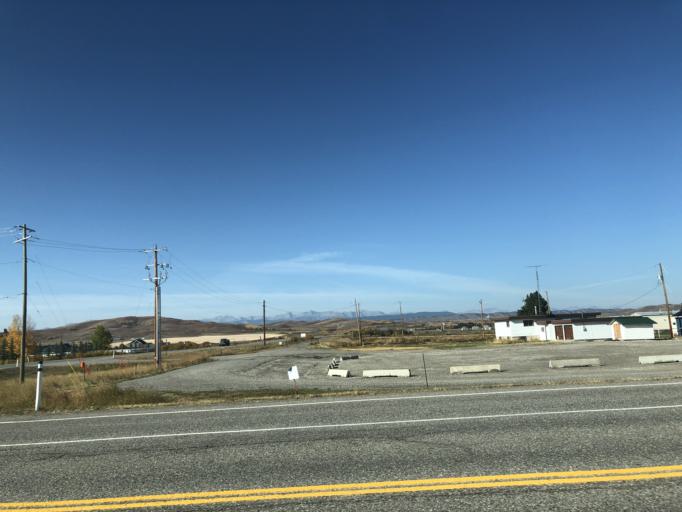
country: CA
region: Alberta
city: Black Diamond
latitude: 50.5355
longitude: -114.2310
